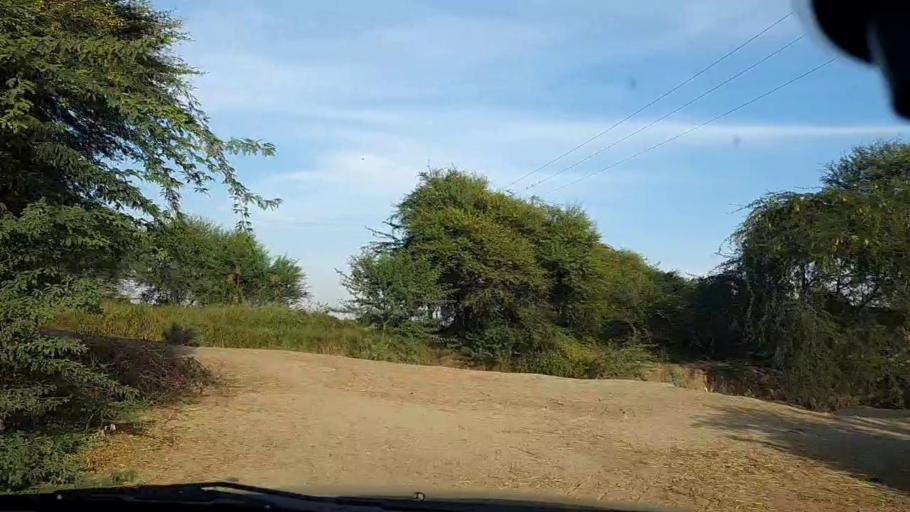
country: PK
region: Sindh
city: Mirpur Batoro
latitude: 24.6528
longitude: 68.2978
